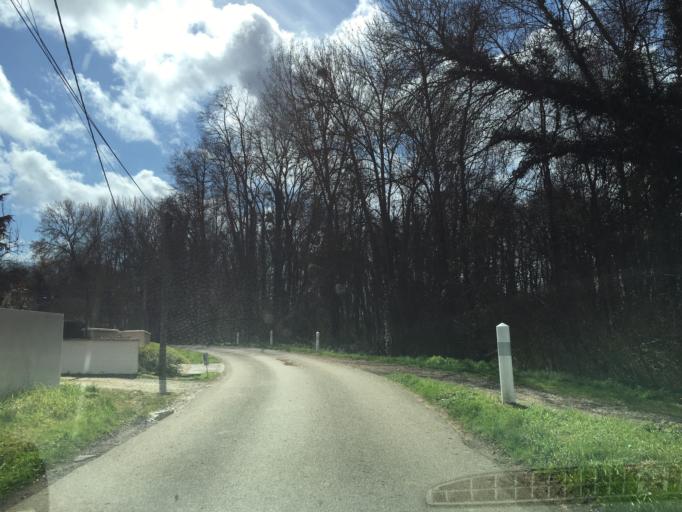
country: FR
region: Bourgogne
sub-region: Departement de l'Yonne
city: Charbuy
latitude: 47.8166
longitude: 3.4229
